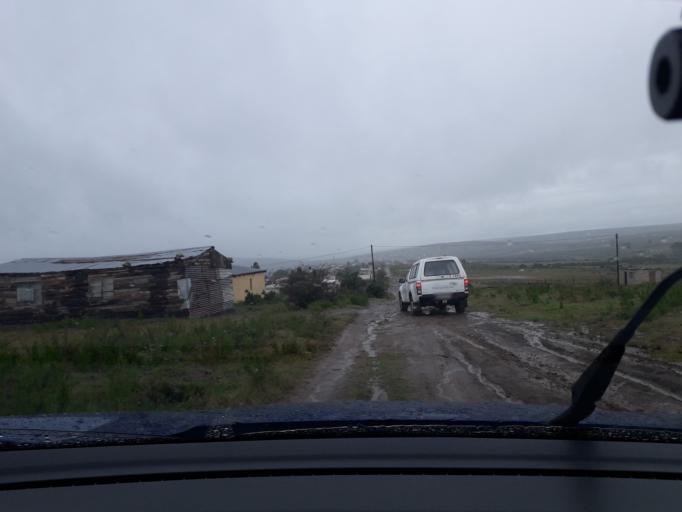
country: ZA
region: Eastern Cape
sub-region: Buffalo City Metropolitan Municipality
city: Bhisho
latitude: -32.8061
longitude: 27.3636
